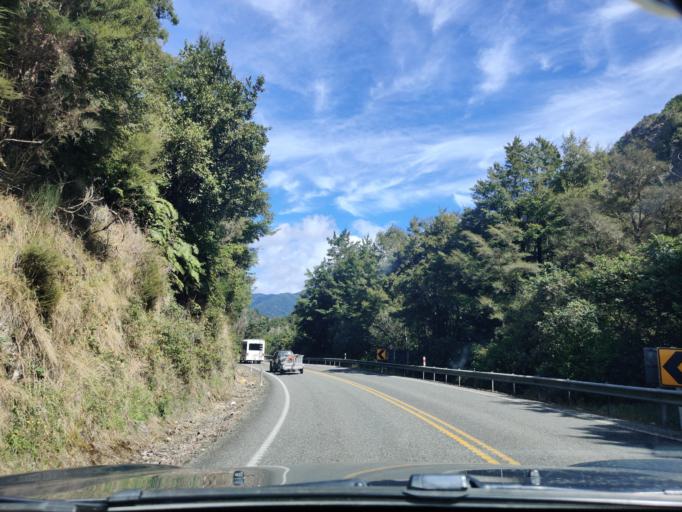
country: NZ
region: West Coast
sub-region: Buller District
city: Westport
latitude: -41.7688
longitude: 172.2311
